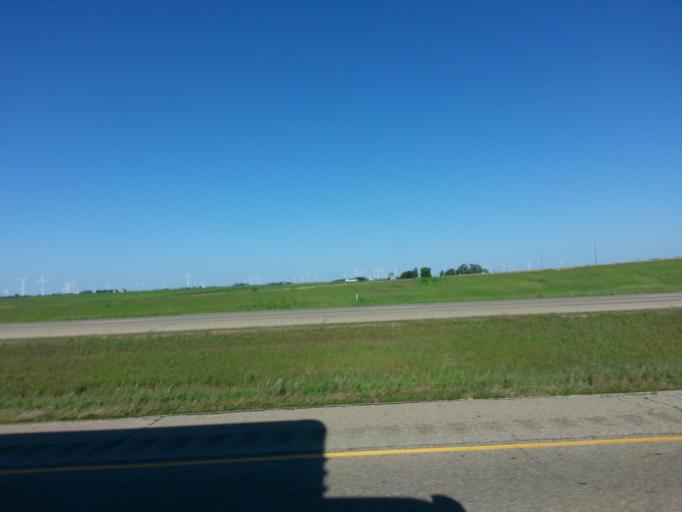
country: US
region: Illinois
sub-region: Woodford County
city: Minonk
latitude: 40.8546
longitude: -89.0365
